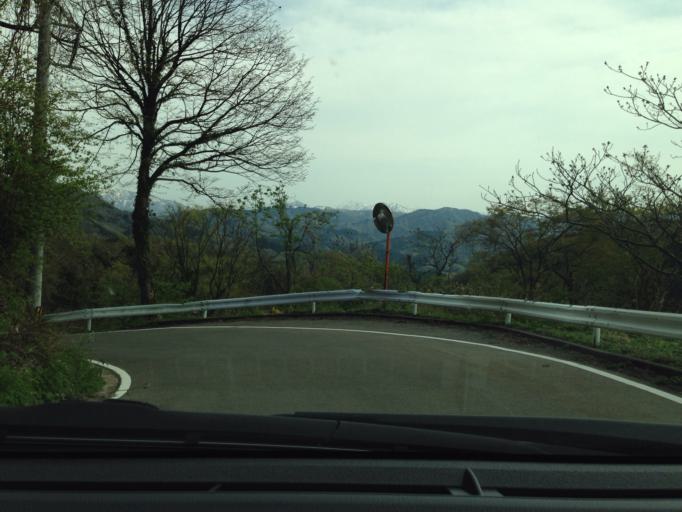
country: JP
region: Toyama
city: Fukumitsu
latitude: 36.5213
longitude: 136.7625
